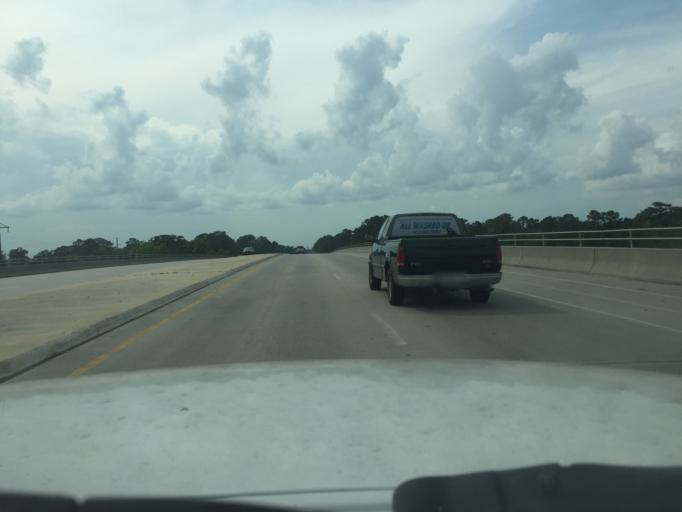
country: US
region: Georgia
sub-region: Chatham County
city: Whitemarsh Island
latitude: 32.0346
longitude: -80.9854
